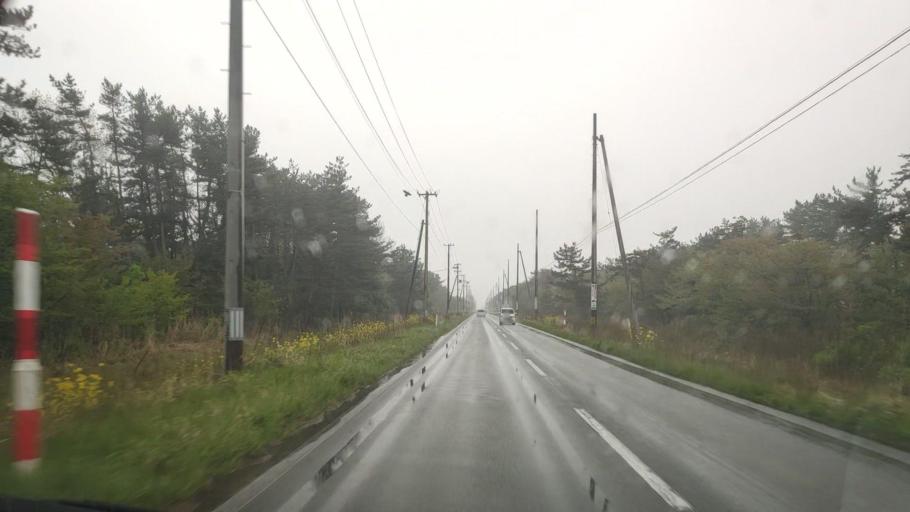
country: JP
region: Akita
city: Tenno
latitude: 40.0089
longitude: 139.9510
